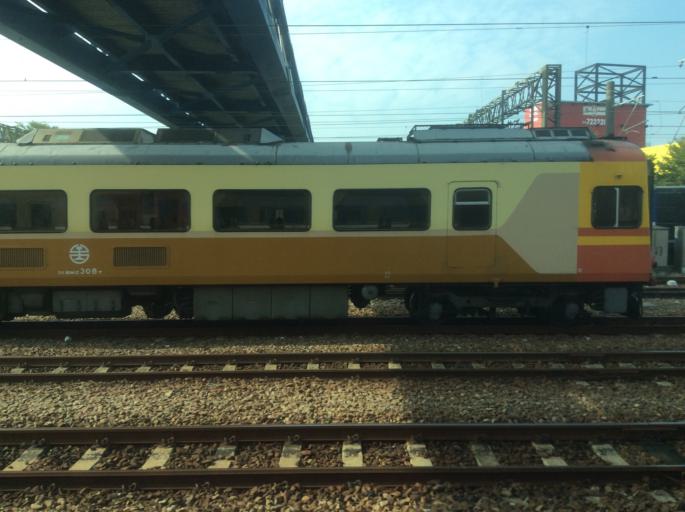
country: TW
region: Taiwan
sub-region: Changhua
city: Chang-hua
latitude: 24.0822
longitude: 120.5381
